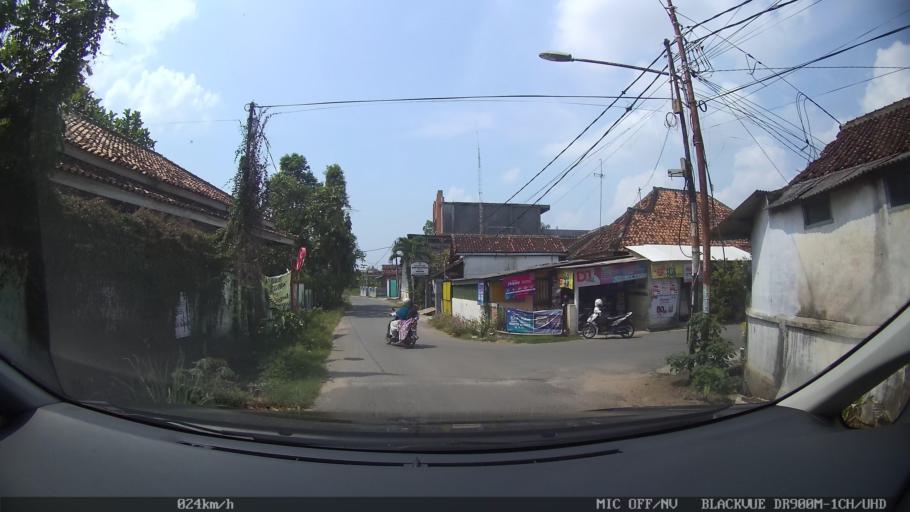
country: ID
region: Lampung
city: Pringsewu
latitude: -5.3587
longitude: 104.9758
